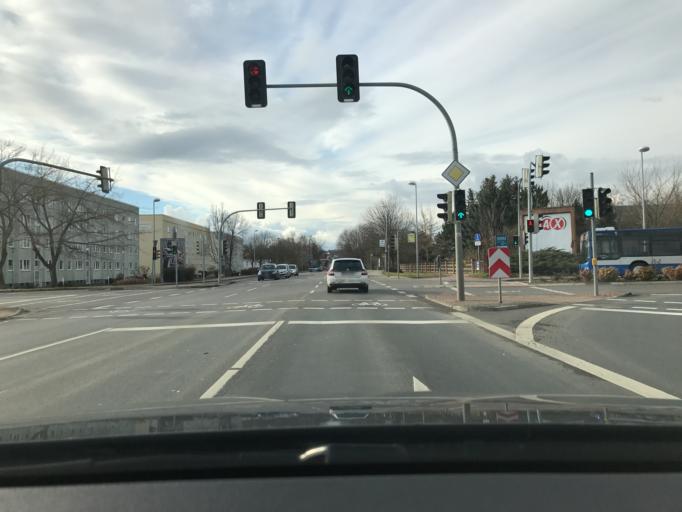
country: DE
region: Saxony-Anhalt
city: Erdeborn
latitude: 51.5086
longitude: 11.5848
